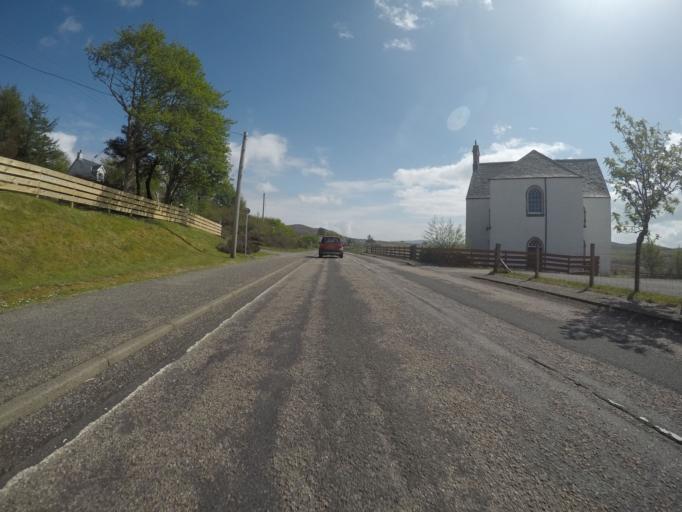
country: GB
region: Scotland
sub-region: Highland
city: Portree
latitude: 57.4826
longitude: -6.3039
